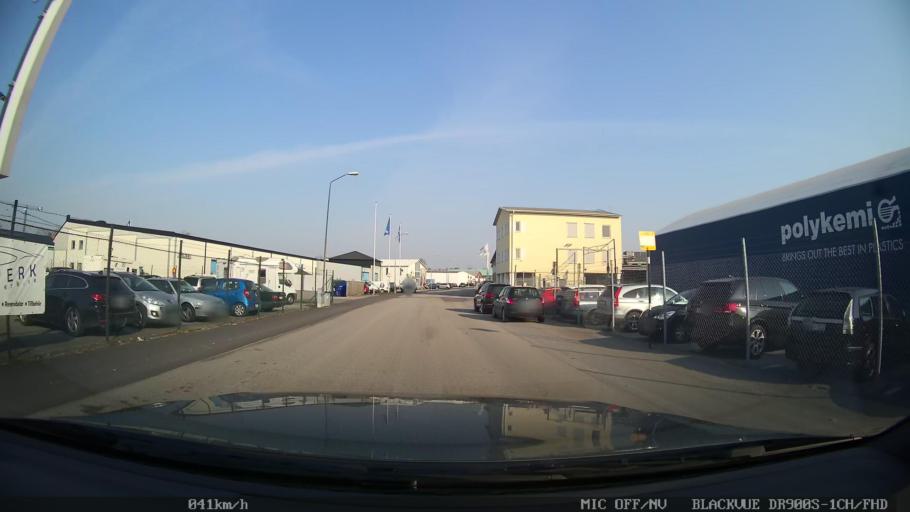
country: SE
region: Skane
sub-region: Ystads Kommun
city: Ystad
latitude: 55.4375
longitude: 13.8375
